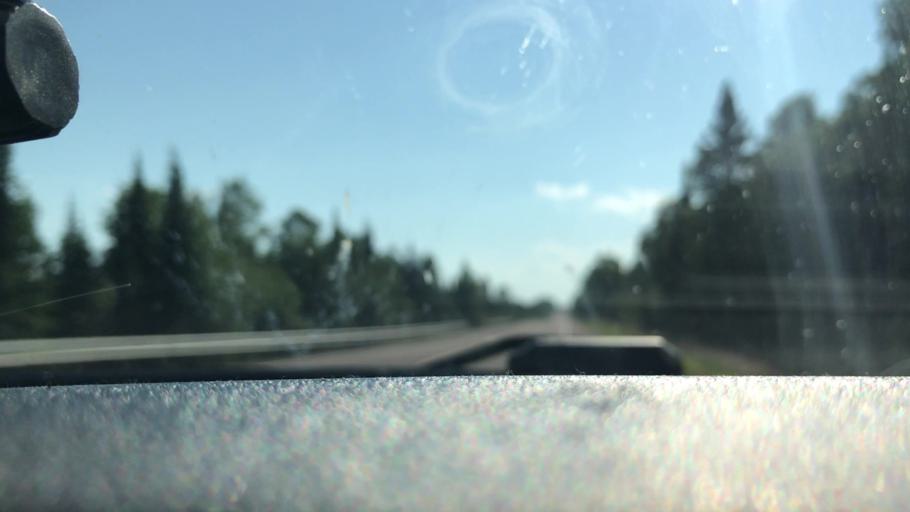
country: US
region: Minnesota
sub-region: Cook County
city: Grand Marais
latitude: 47.8314
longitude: -89.9787
